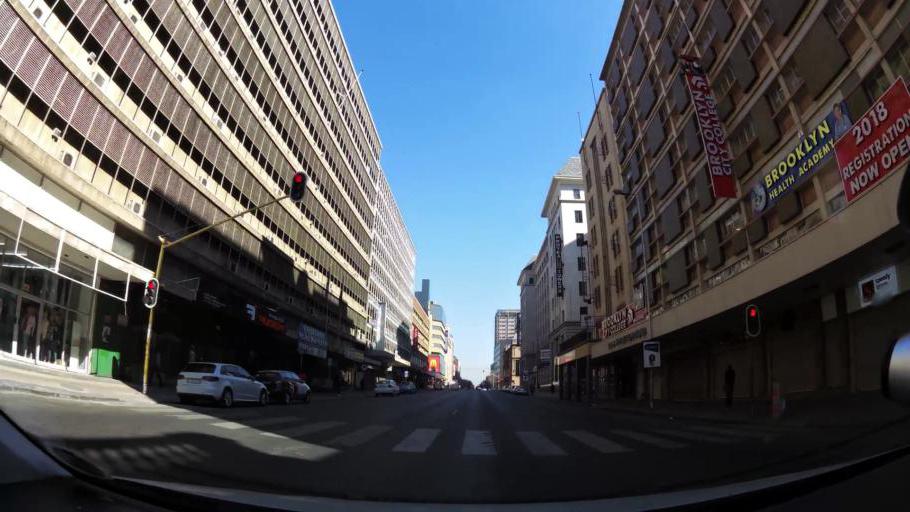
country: ZA
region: Gauteng
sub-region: City of Tshwane Metropolitan Municipality
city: Pretoria
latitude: -25.7478
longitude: 28.1895
